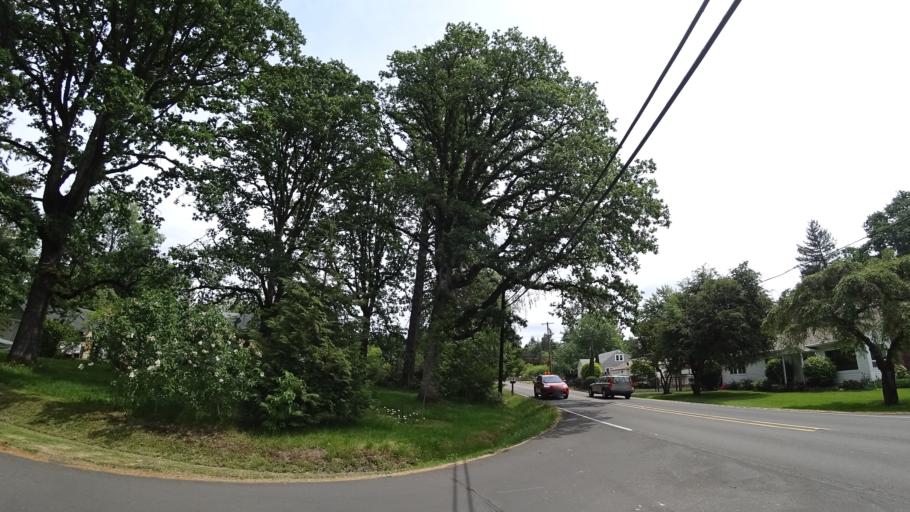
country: US
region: Oregon
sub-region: Washington County
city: Metzger
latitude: 45.4467
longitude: -122.7616
